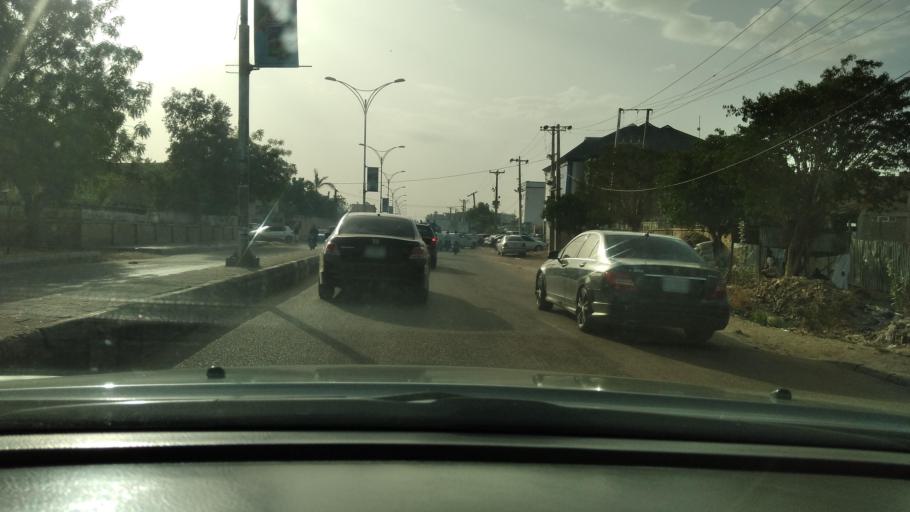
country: NG
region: Kano
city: Kano
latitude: 11.9775
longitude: 8.5648
